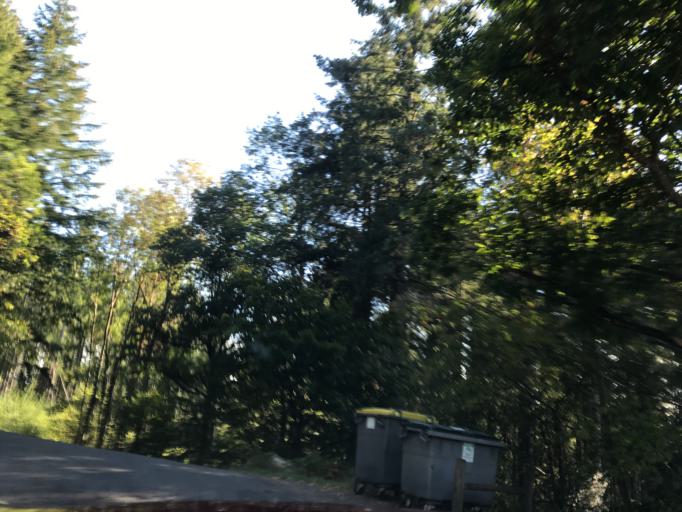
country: FR
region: Auvergne
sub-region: Departement du Puy-de-Dome
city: Escoutoux
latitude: 45.7730
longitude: 3.6142
